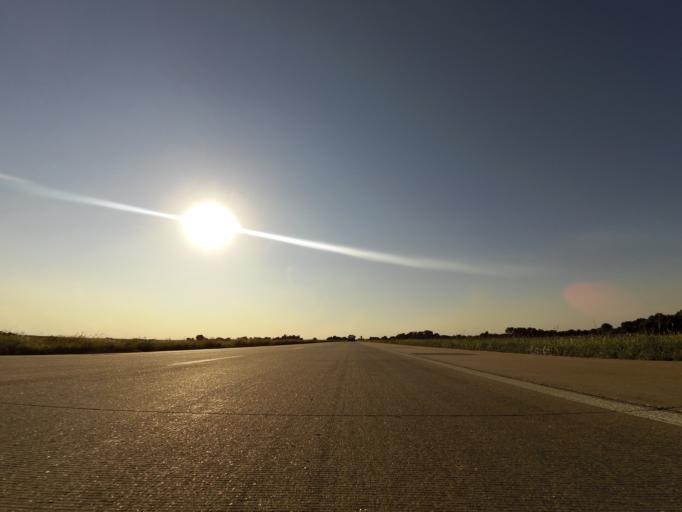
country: US
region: Kansas
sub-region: Sedgwick County
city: Colwich
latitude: 37.8506
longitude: -97.5998
